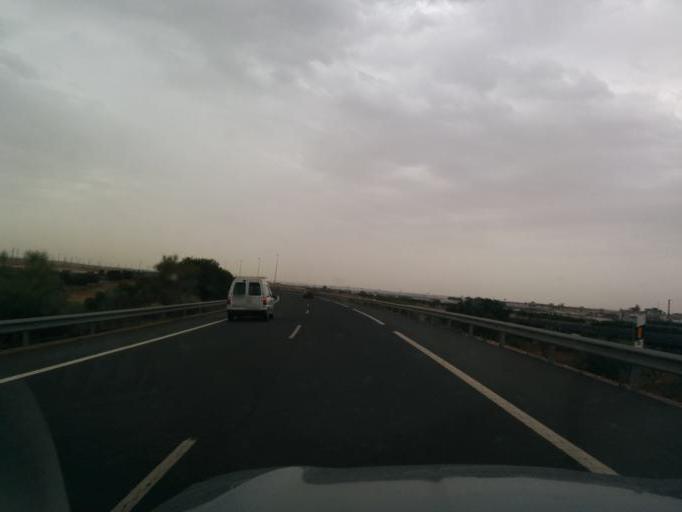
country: ES
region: Andalusia
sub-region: Provincia de Huelva
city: San Juan del Puerto
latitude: 37.3118
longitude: -6.8774
